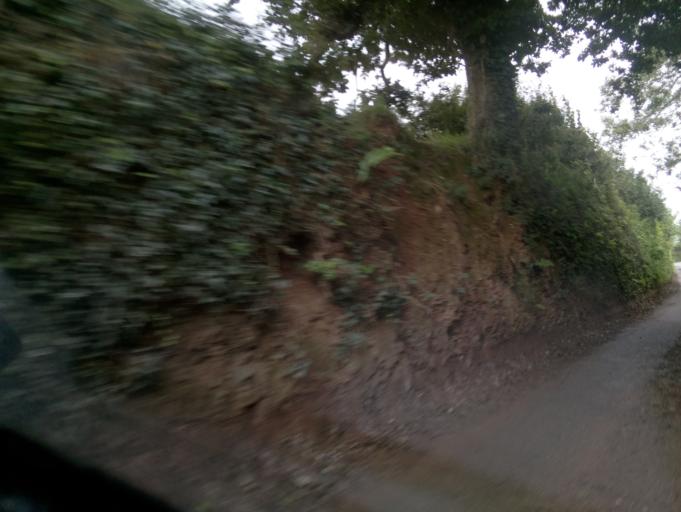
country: GB
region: England
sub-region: Devon
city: Kingsbridge
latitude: 50.2939
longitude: -3.7174
